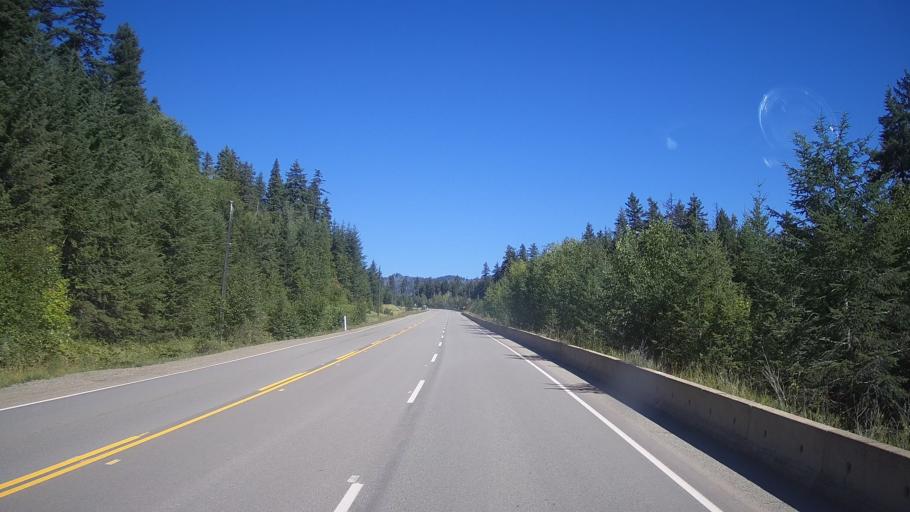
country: CA
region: British Columbia
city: Kamloops
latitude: 51.4623
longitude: -120.2310
